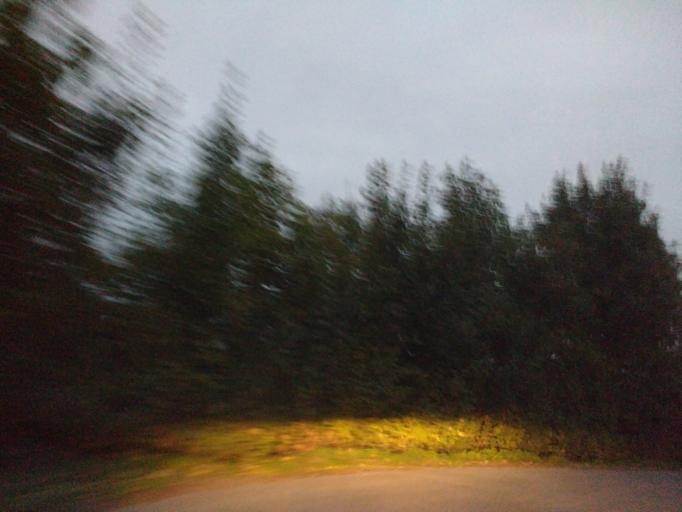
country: DE
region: North Rhine-Westphalia
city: Warstein
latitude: 51.4357
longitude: 8.3882
